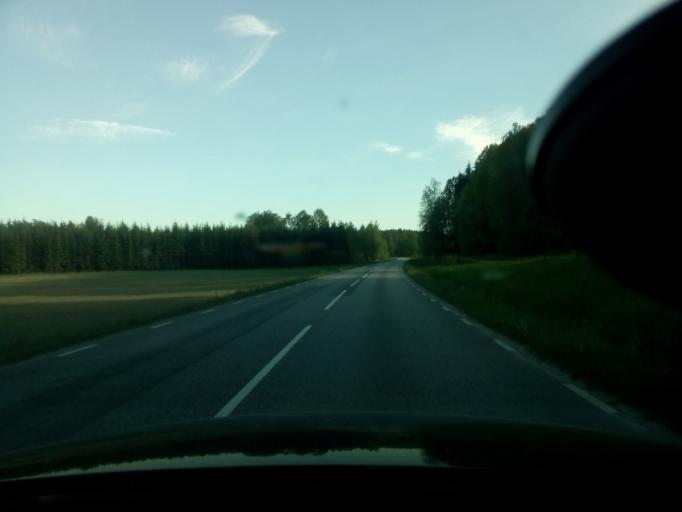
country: SE
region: Soedermanland
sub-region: Nykopings Kommun
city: Nykoping
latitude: 58.7883
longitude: 17.0048
